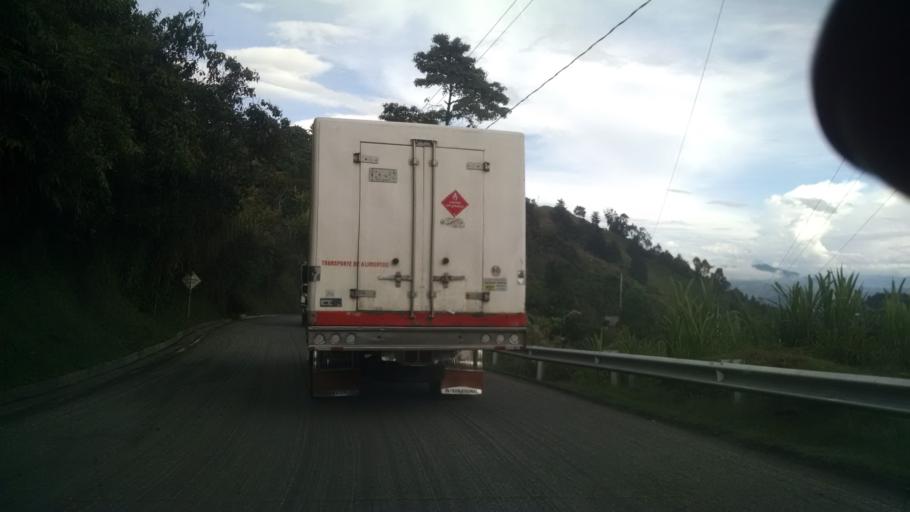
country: CO
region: Antioquia
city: Santa Barbara
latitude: 5.9149
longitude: -75.5779
